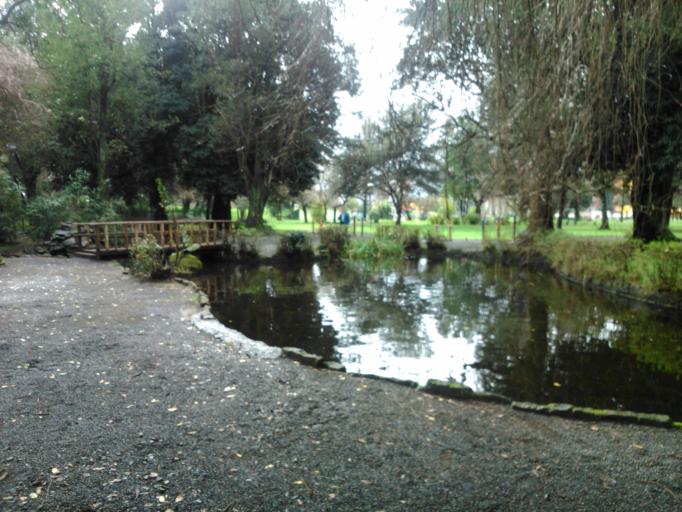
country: CL
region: Araucania
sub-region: Provincia de Cautin
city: Temuco
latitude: -38.7422
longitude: -72.6224
